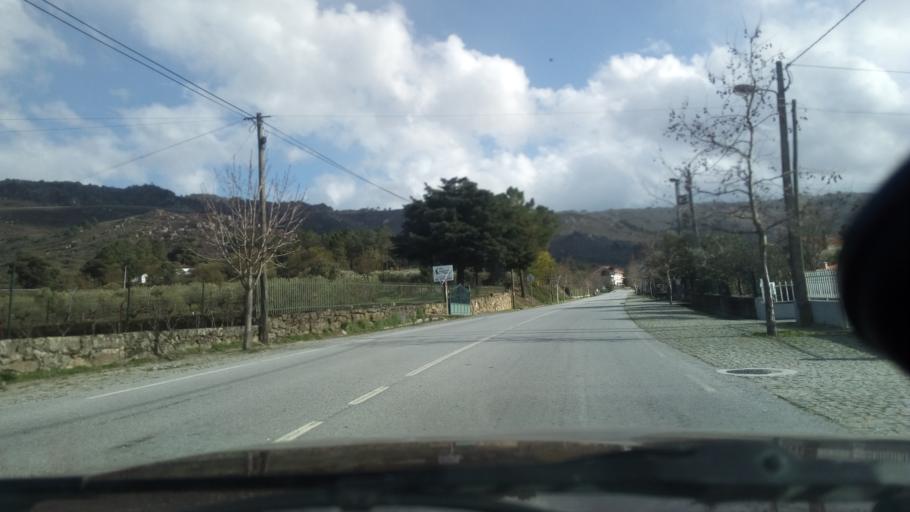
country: PT
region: Guarda
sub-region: Guarda
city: Guarda
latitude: 40.6010
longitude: -7.2929
